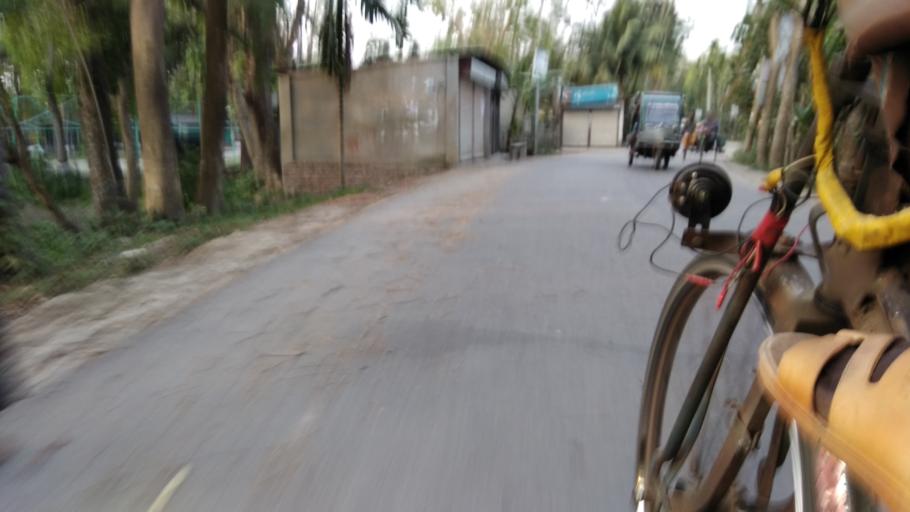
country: BD
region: Barisal
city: Mehendiganj
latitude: 22.9368
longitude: 90.4073
